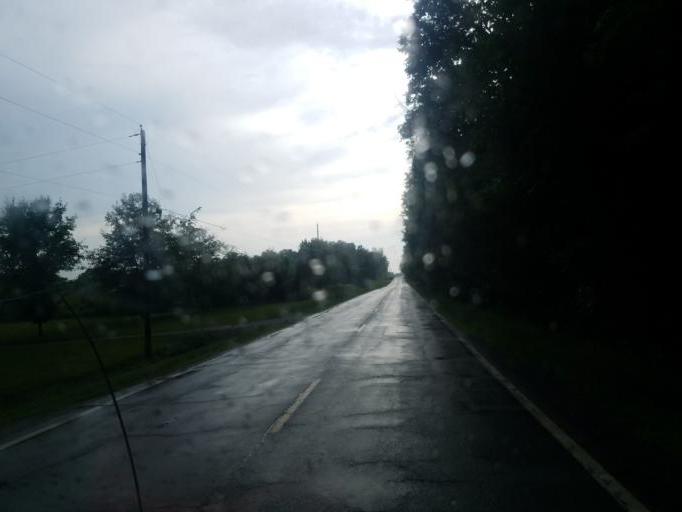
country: US
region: Ohio
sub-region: Wayne County
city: Creston
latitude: 40.9445
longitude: -81.9683
